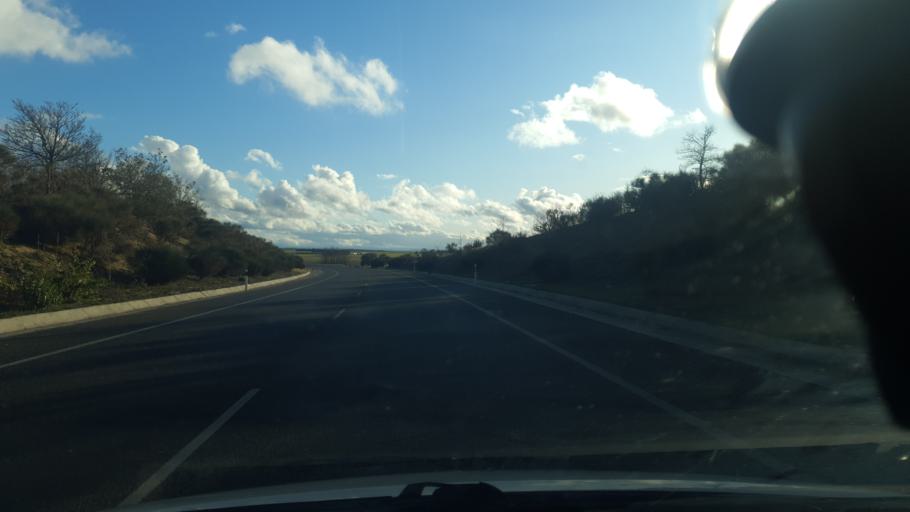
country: ES
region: Castille and Leon
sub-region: Provincia de Segovia
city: Codorniz
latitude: 41.0429
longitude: -4.6228
